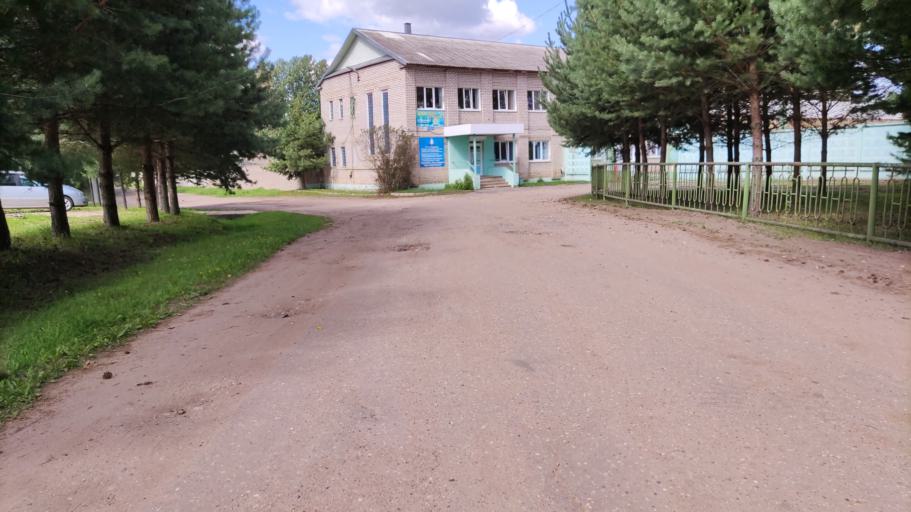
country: RU
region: Tverskaya
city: Rzhev
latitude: 56.2367
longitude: 34.3309
